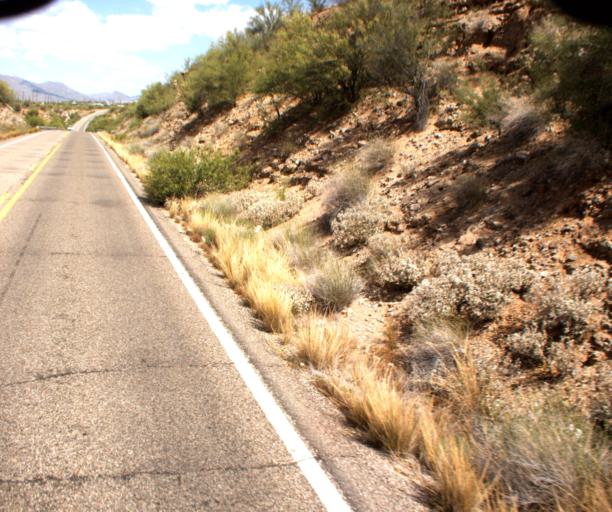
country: US
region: Arizona
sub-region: Pinal County
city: Kearny
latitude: 33.0713
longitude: -110.9175
